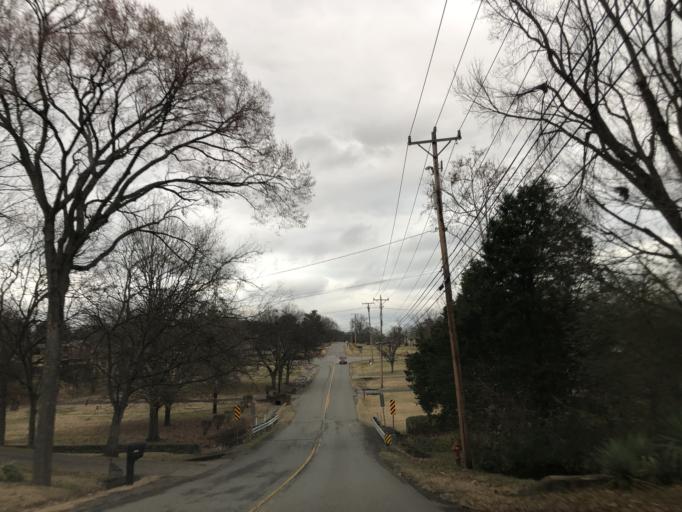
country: US
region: Tennessee
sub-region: Davidson County
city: Goodlettsville
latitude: 36.2971
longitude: -86.6896
